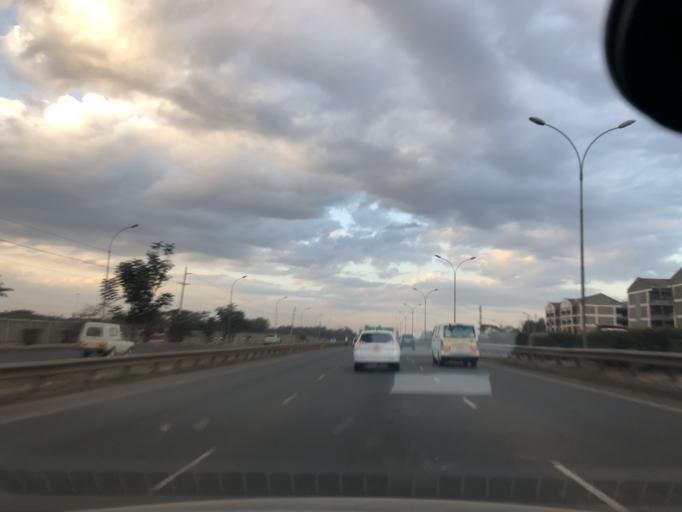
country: KE
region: Kiambu
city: Kiambu
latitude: -1.1930
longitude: 36.9269
